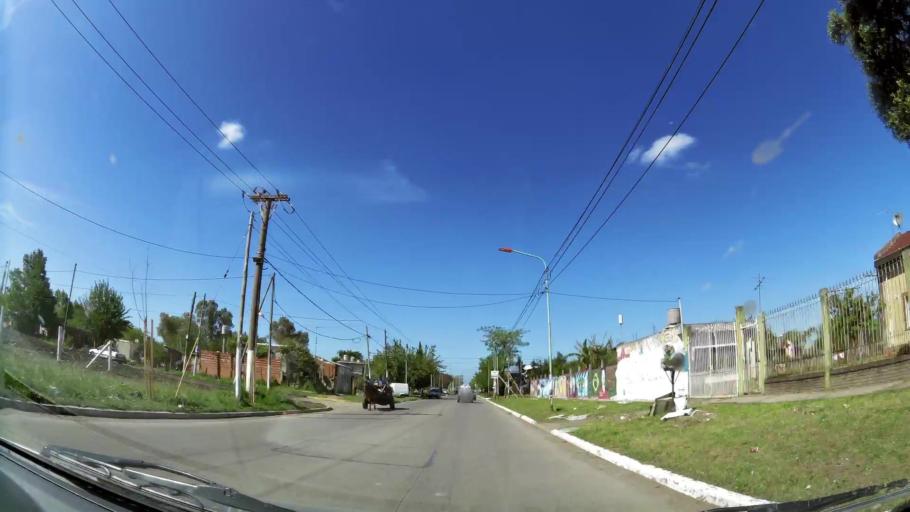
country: AR
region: Buenos Aires
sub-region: Partido de Quilmes
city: Quilmes
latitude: -34.7966
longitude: -58.2573
